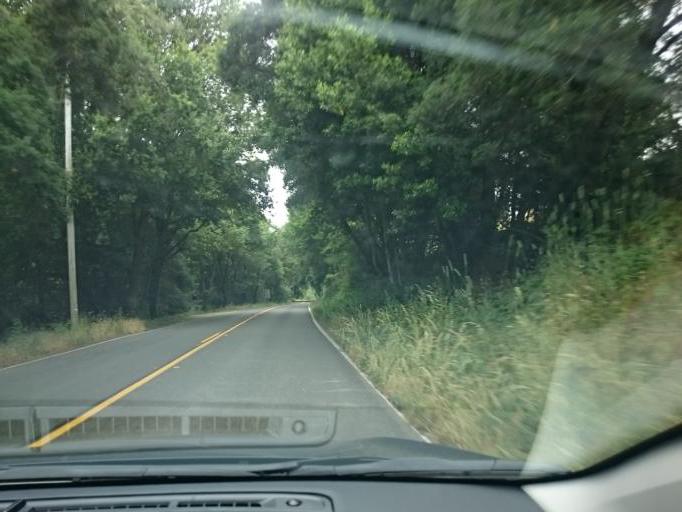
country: US
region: California
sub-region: Marin County
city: Lagunitas-Forest Knolls
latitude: 38.0356
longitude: -122.7833
